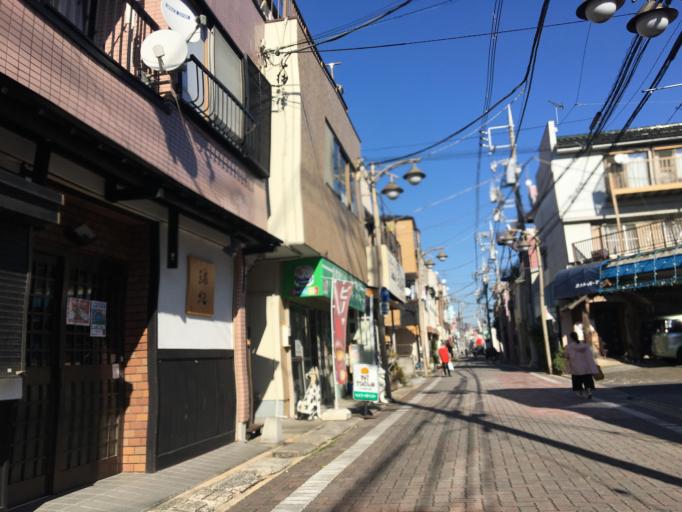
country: JP
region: Tokyo
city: Urayasu
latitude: 35.6868
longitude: 139.9023
